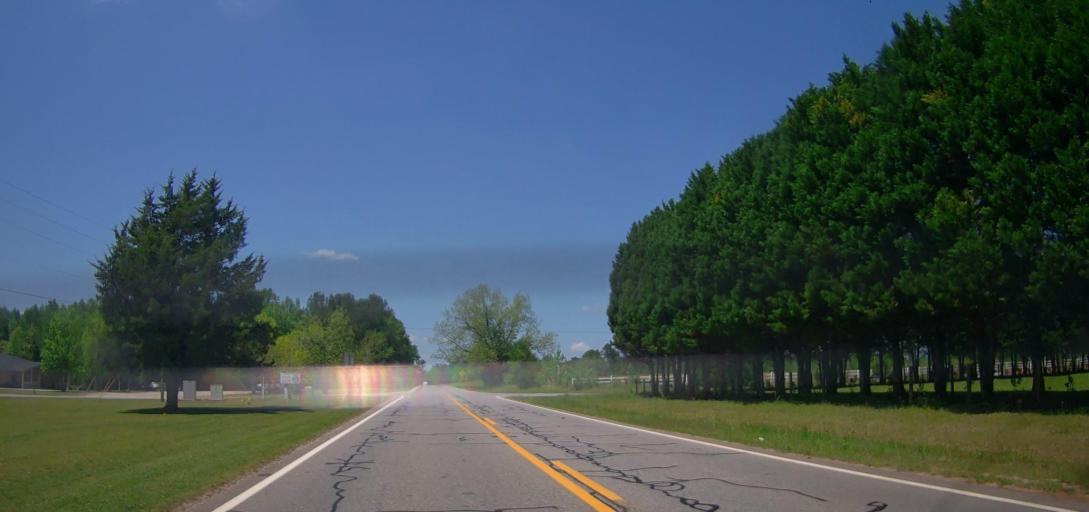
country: US
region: Georgia
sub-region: Jasper County
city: Monticello
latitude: 33.3183
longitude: -83.7164
